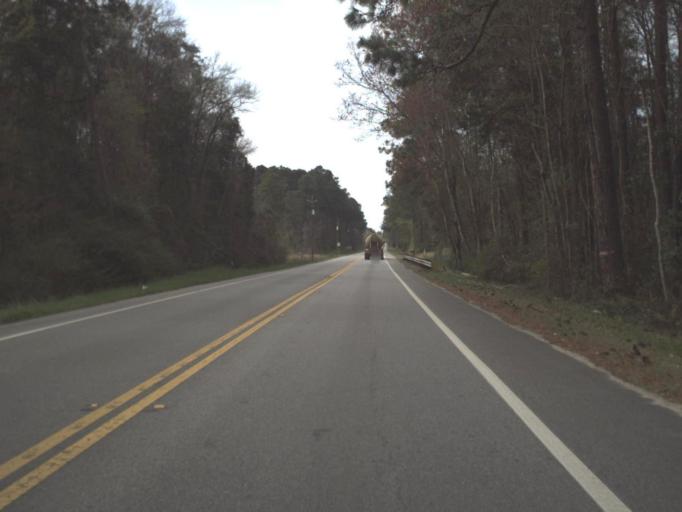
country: US
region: Florida
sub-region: Holmes County
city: Bonifay
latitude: 30.8174
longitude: -85.6713
